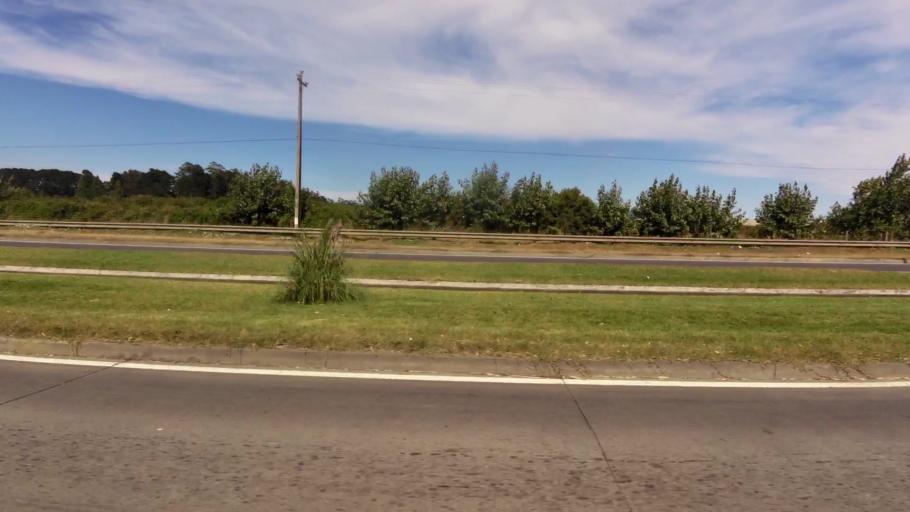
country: CL
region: Biobio
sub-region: Provincia de Concepcion
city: Talcahuano
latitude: -36.7642
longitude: -73.1172
